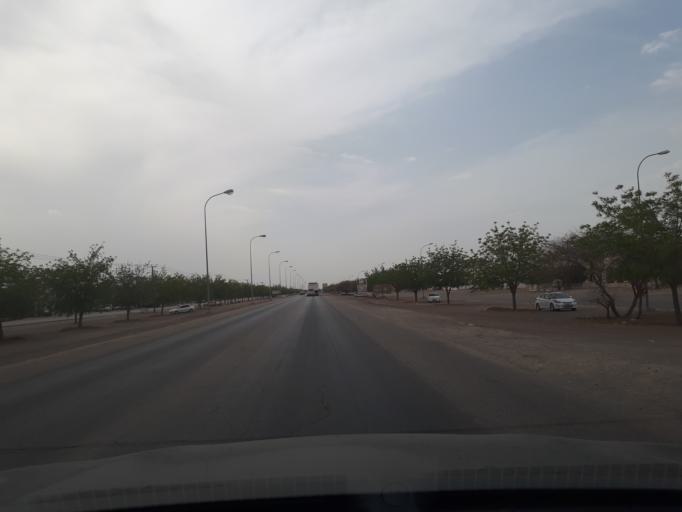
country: OM
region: Ash Sharqiyah
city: Badiyah
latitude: 22.4565
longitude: 58.8040
